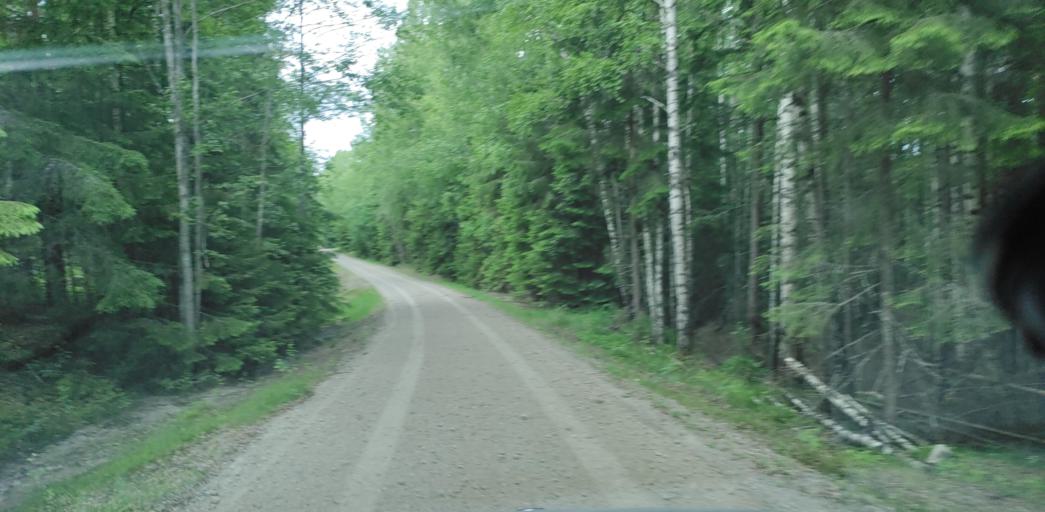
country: SE
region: Vaermland
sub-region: Munkfors Kommun
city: Munkfors
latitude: 59.9665
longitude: 13.4199
